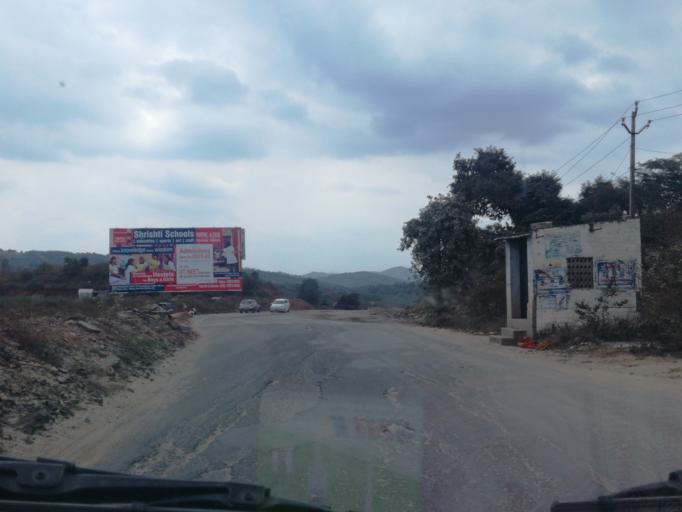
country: IN
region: Andhra Pradesh
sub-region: Chittoor
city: Ramapuram
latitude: 13.0877
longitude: 79.1351
